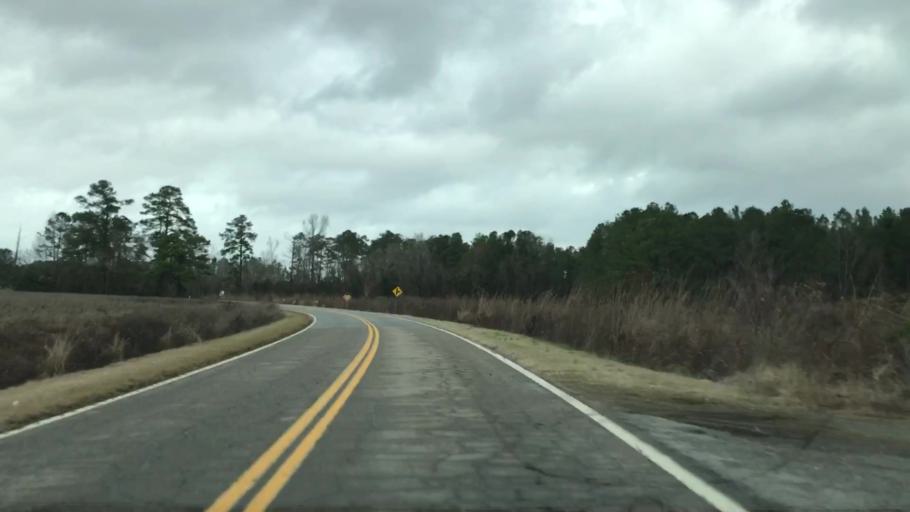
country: US
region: South Carolina
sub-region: Florence County
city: Johnsonville
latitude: 33.6592
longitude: -79.3042
